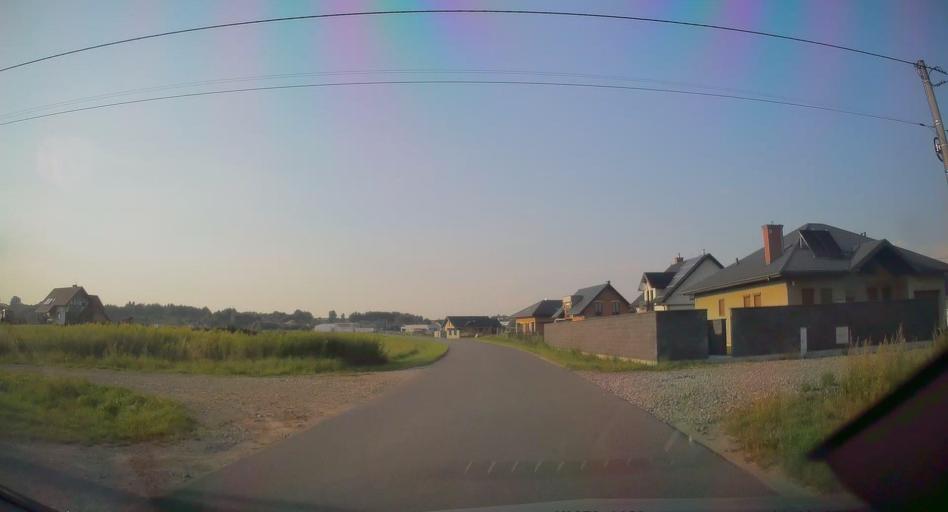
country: PL
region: Subcarpathian Voivodeship
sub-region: Powiat debicki
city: Zyrakow
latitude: 50.0844
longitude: 21.3828
